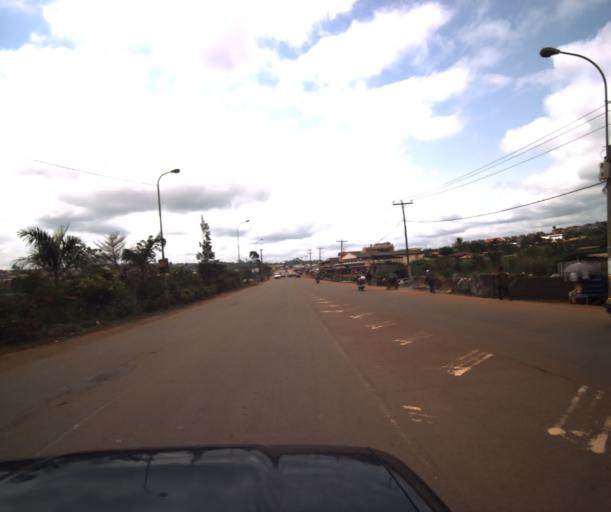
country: CM
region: Centre
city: Yaounde
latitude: 3.8100
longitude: 11.5106
